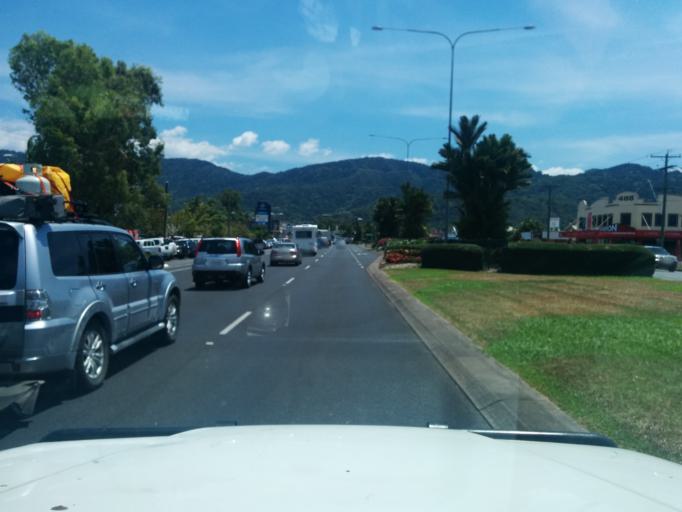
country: AU
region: Queensland
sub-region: Cairns
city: Woree
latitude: -16.9417
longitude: 145.7406
